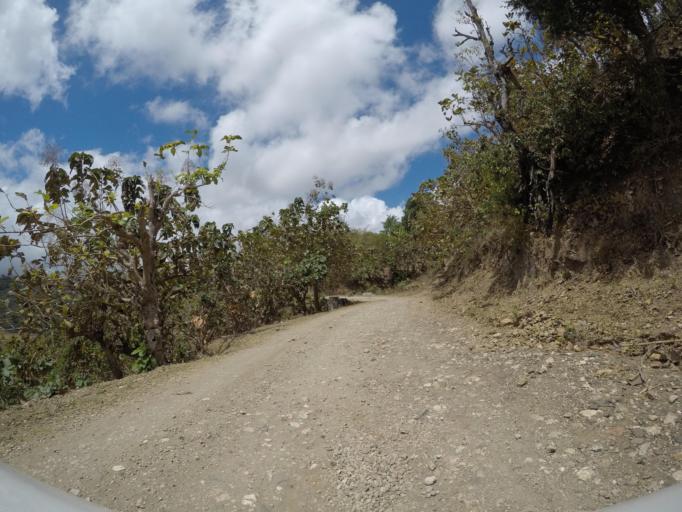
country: TL
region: Lautem
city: Lospalos
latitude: -8.5408
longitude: 126.8372
